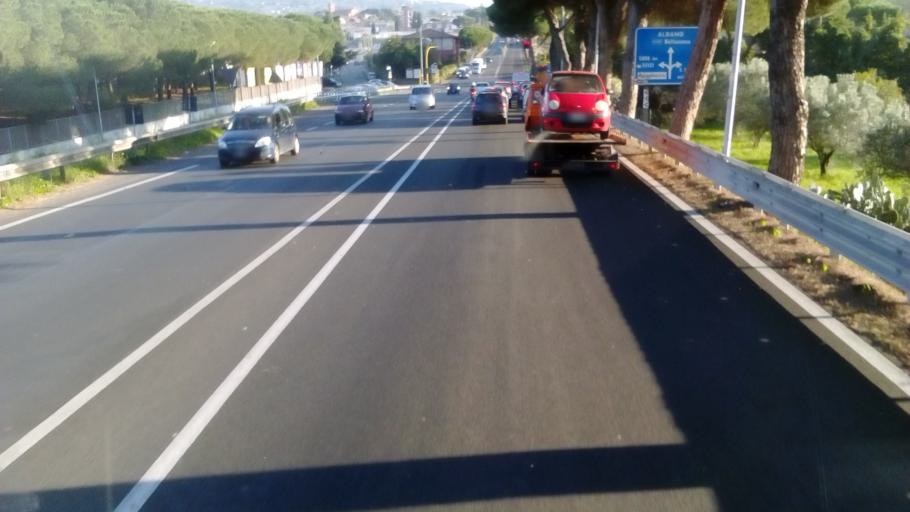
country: IT
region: Latium
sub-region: Citta metropolitana di Roma Capitale
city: Ciampino
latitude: 41.7763
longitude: 12.6073
